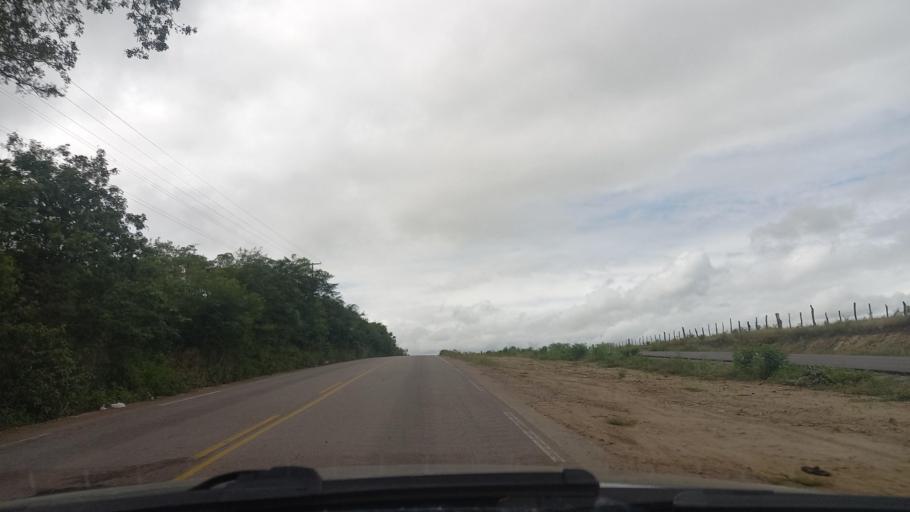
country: BR
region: Alagoas
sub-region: Batalha
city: Batalha
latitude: -9.6447
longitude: -37.1903
